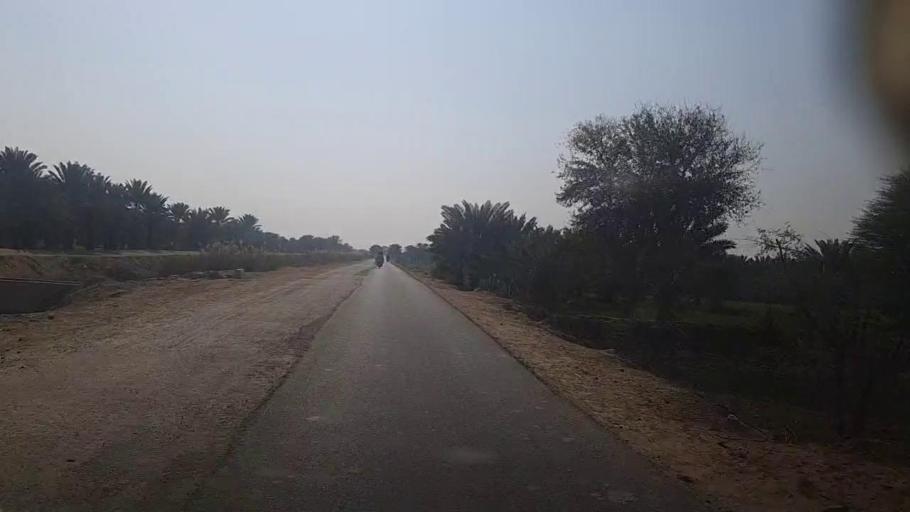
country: PK
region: Sindh
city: Khairpur
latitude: 27.4661
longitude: 68.8184
